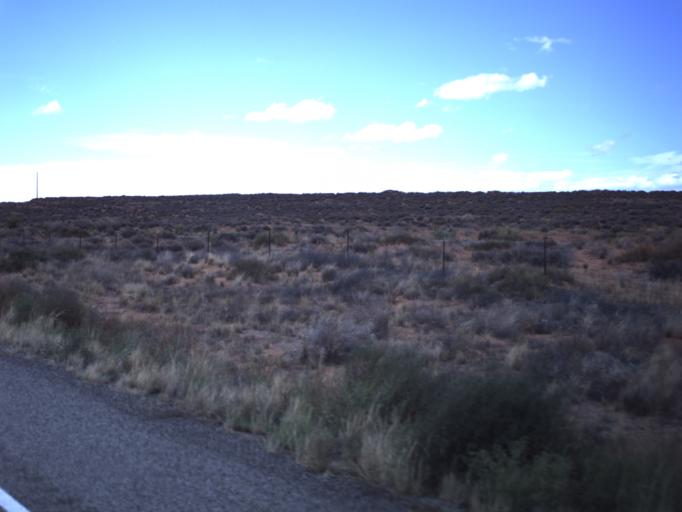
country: US
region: Utah
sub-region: San Juan County
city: Blanding
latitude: 37.2648
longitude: -109.6340
